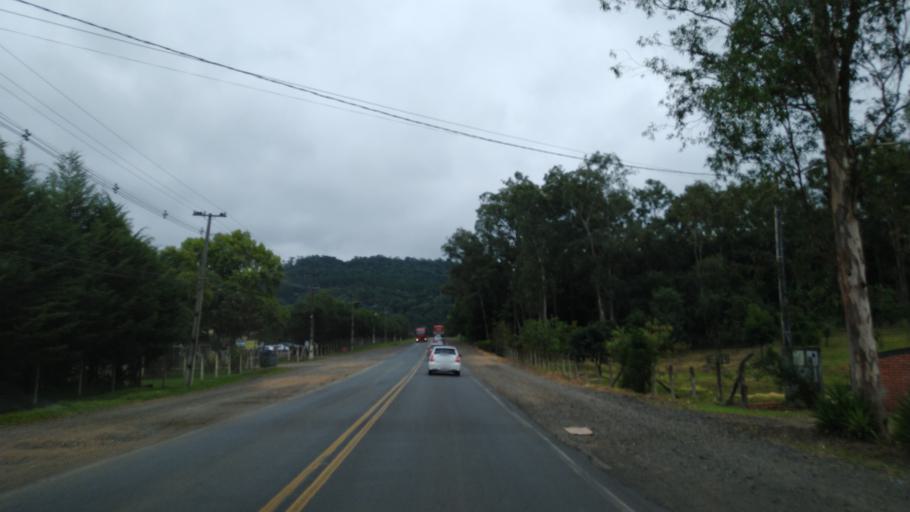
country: BR
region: Parana
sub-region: Uniao Da Vitoria
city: Uniao da Vitoria
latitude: -26.2354
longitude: -51.1257
